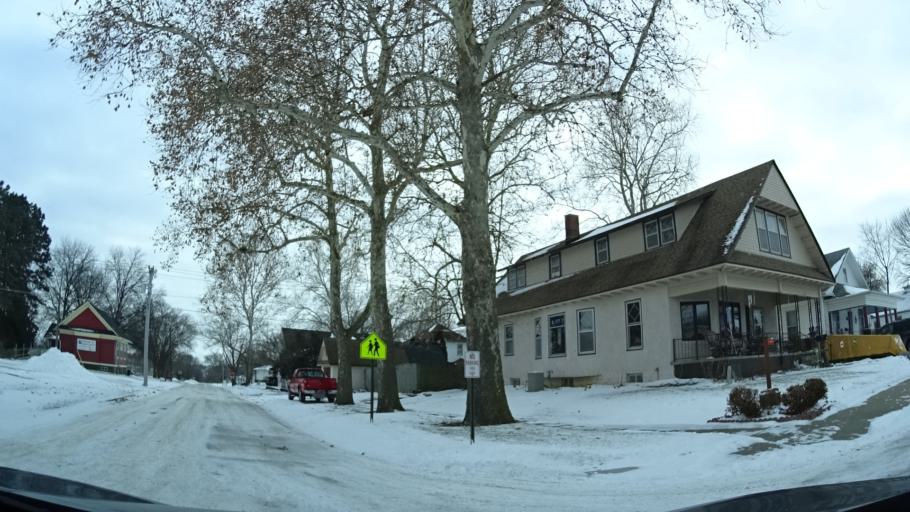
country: US
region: Nebraska
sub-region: Otoe County
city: Nebraska City
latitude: 40.6767
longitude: -95.8640
